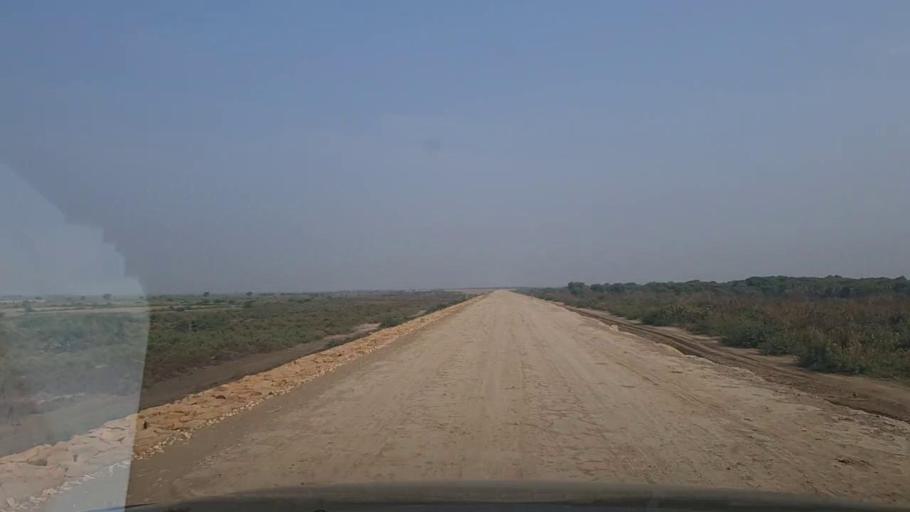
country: PK
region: Sindh
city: Bulri
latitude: 24.9482
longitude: 68.2896
